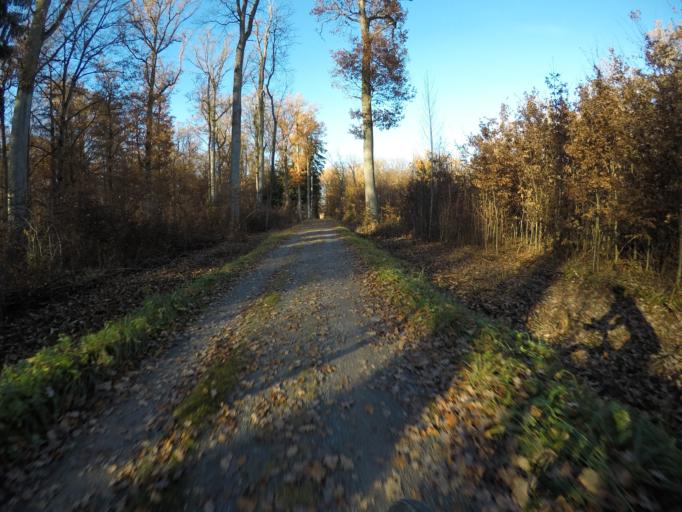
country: DE
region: Baden-Wuerttemberg
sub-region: Regierungsbezirk Stuttgart
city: Ehningen
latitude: 48.6790
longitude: 8.9592
